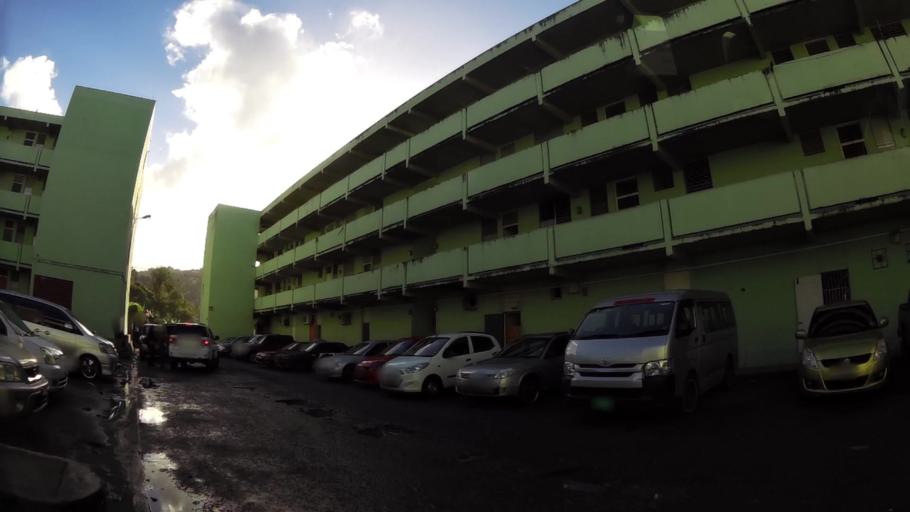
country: LC
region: Castries Quarter
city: Bisee
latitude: 14.0128
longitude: -60.9884
